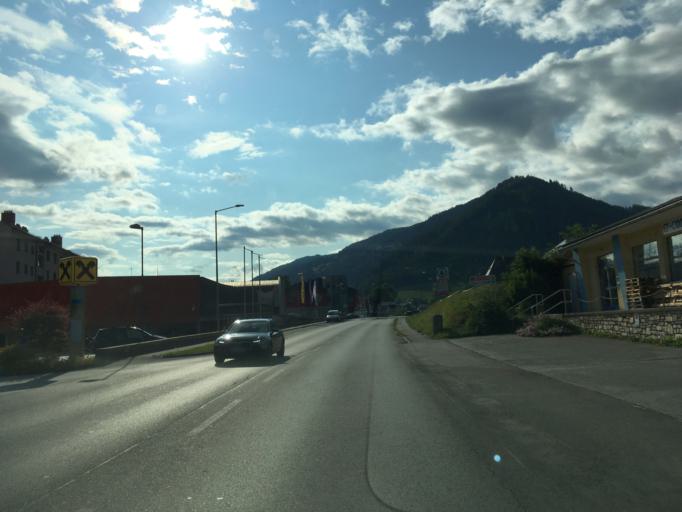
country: AT
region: Styria
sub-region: Politischer Bezirk Murau
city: Murau
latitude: 47.1123
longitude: 14.1808
